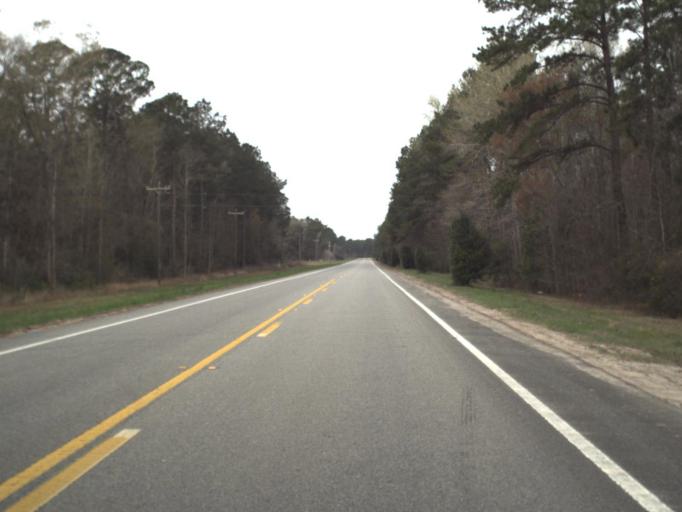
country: US
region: Florida
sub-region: Jefferson County
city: Monticello
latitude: 30.4932
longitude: -83.7346
